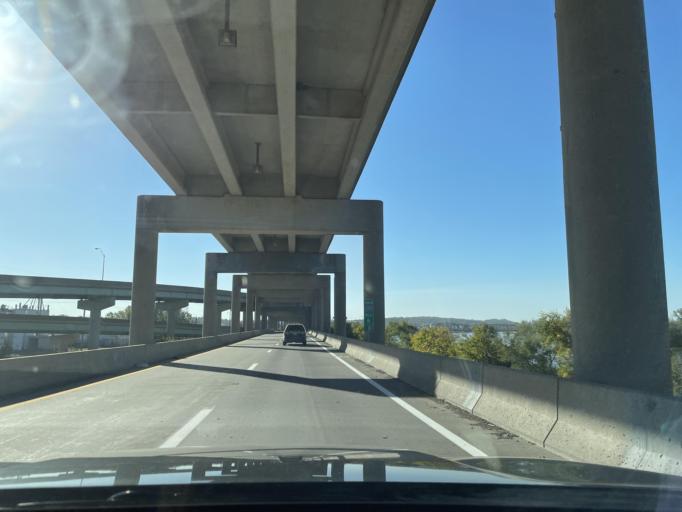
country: US
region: Missouri
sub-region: Buchanan County
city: Saint Joseph
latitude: 39.7645
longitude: -94.8596
